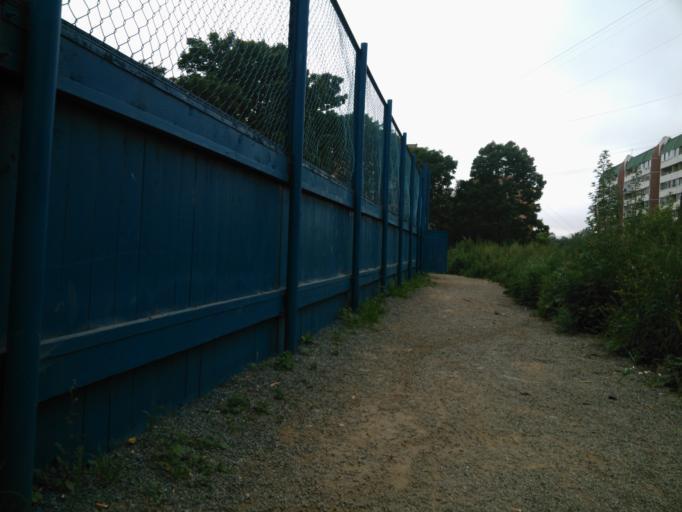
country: RU
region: Primorskiy
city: Vladivostok
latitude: 43.0926
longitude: 131.9648
